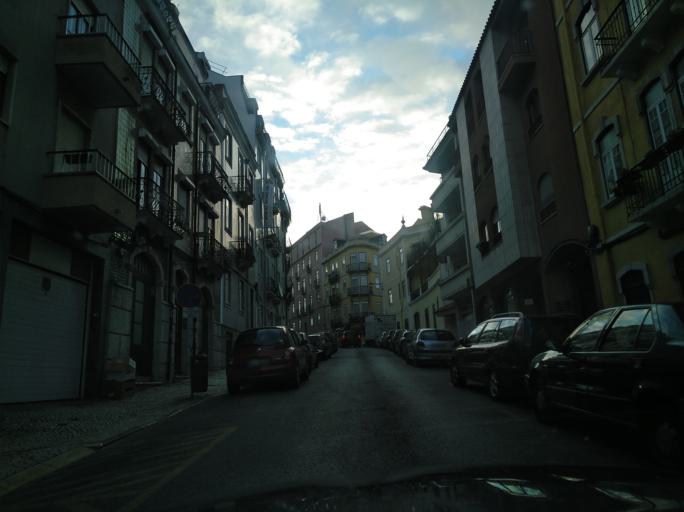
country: PT
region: Lisbon
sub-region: Lisbon
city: Lisbon
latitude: 38.7202
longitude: -9.1325
